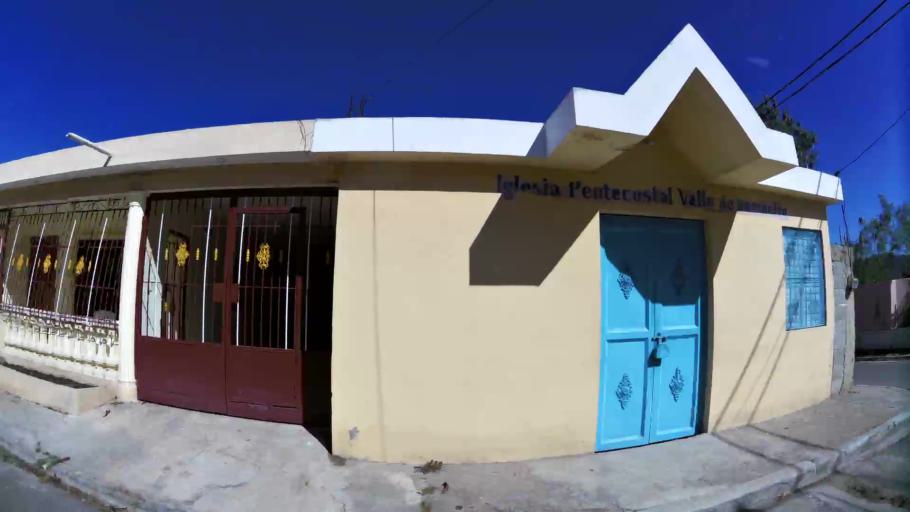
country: DO
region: San Cristobal
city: San Cristobal
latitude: 18.4326
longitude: -70.1225
